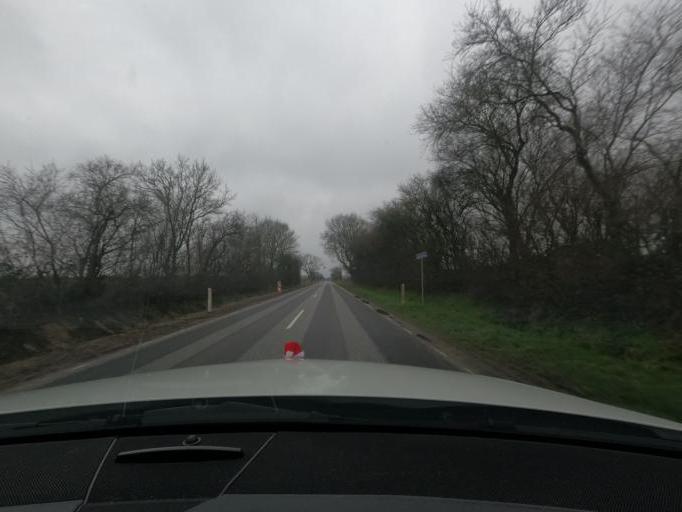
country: DK
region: South Denmark
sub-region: Haderslev Kommune
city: Starup
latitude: 55.2278
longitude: 9.6329
